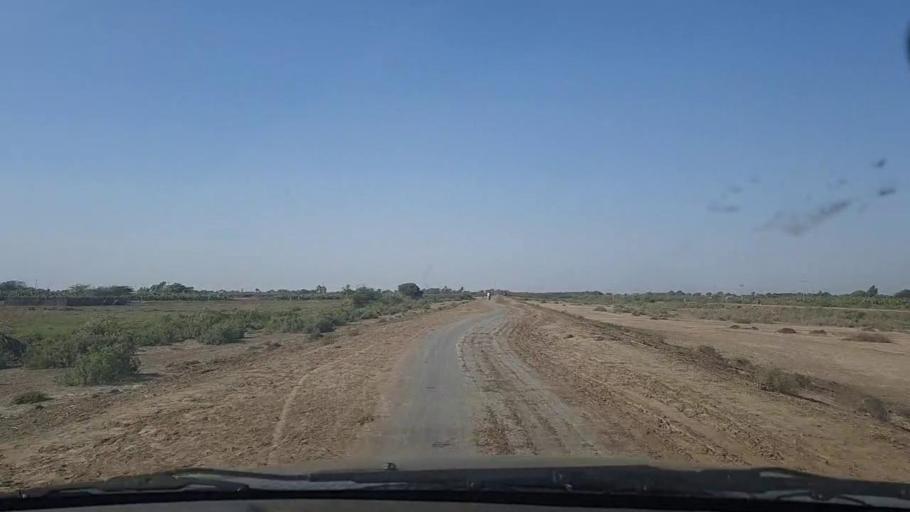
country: PK
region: Sindh
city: Chuhar Jamali
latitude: 24.3206
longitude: 67.7546
